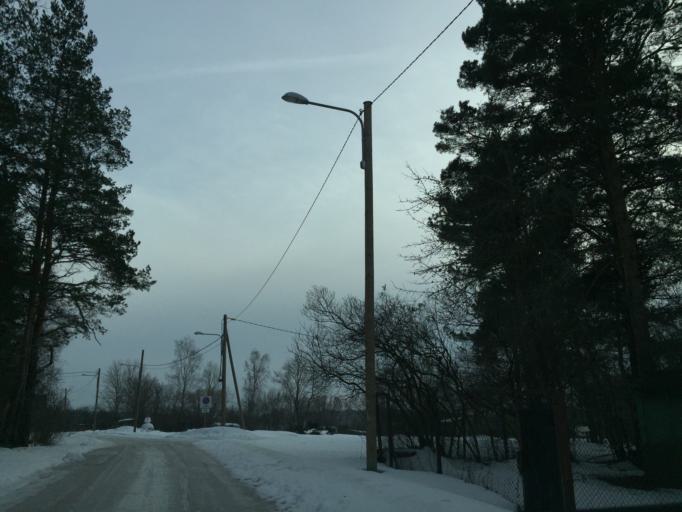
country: LV
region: Salaspils
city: Salaspils
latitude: 56.8436
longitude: 24.4307
